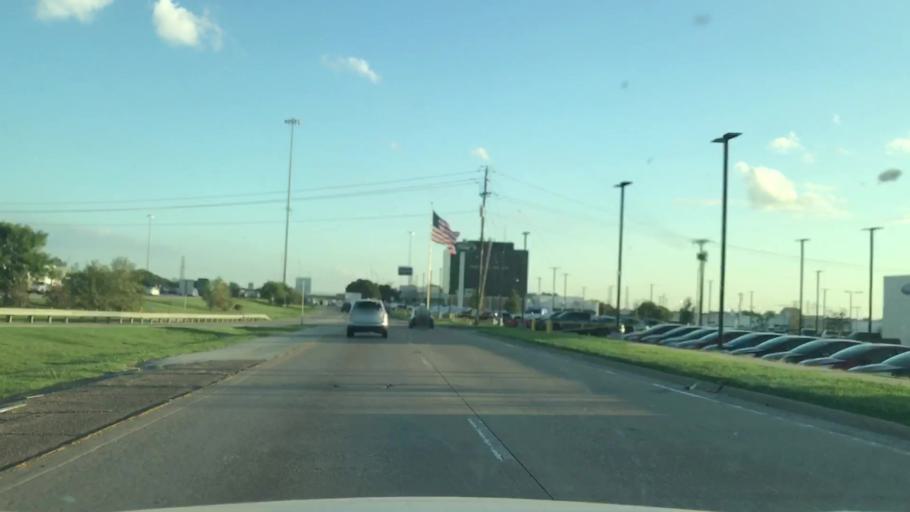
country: US
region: Texas
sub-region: Dallas County
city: Mesquite
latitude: 32.8072
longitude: -96.6279
